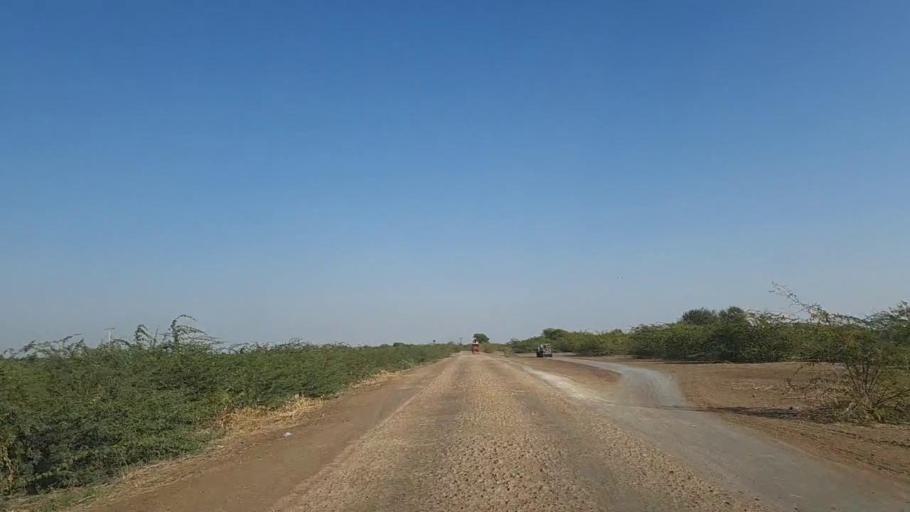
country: PK
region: Sindh
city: Naukot
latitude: 24.9462
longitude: 69.3371
